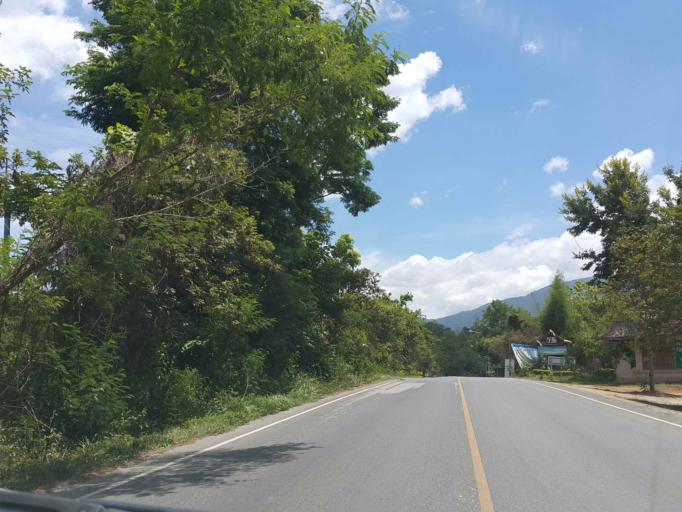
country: TH
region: Chiang Mai
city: Hang Dong
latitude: 18.7393
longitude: 98.8894
